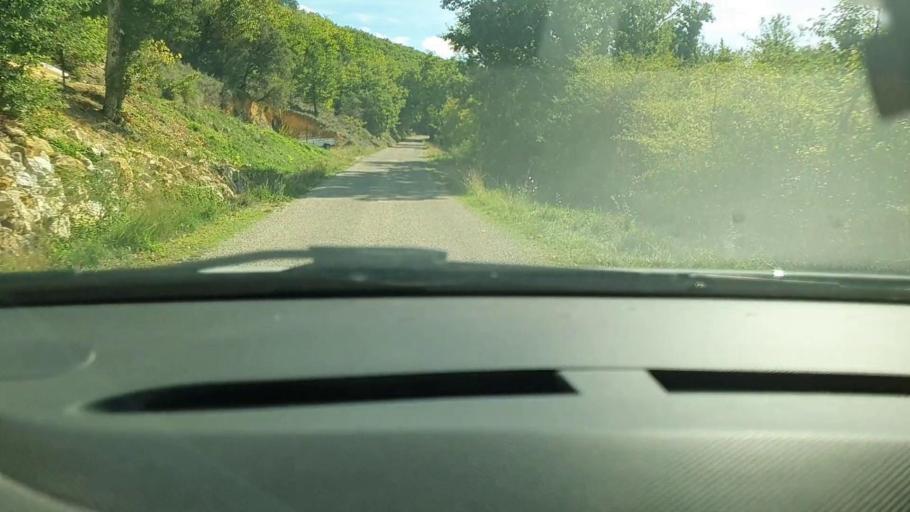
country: FR
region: Languedoc-Roussillon
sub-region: Departement du Gard
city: Saint-Ambroix
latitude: 44.2243
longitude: 4.2845
